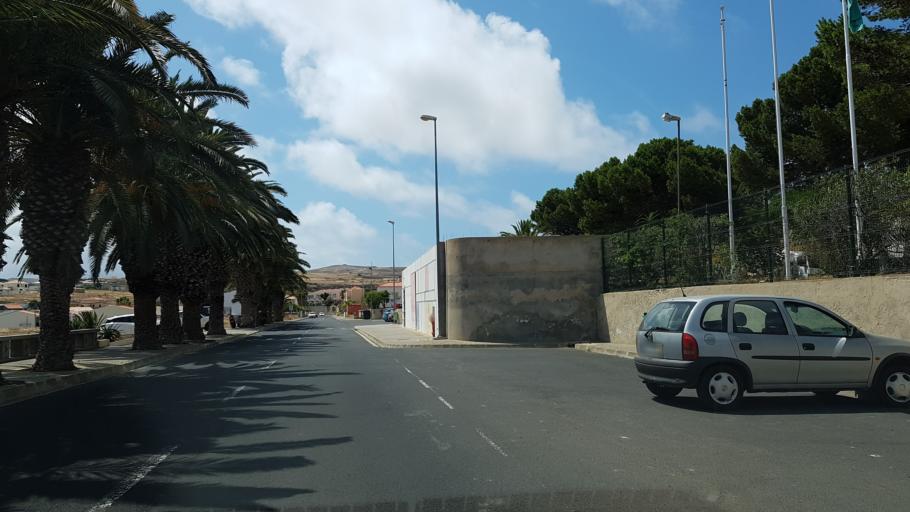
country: PT
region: Madeira
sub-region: Porto Santo
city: Vila de Porto Santo
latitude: 33.0600
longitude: -16.3393
